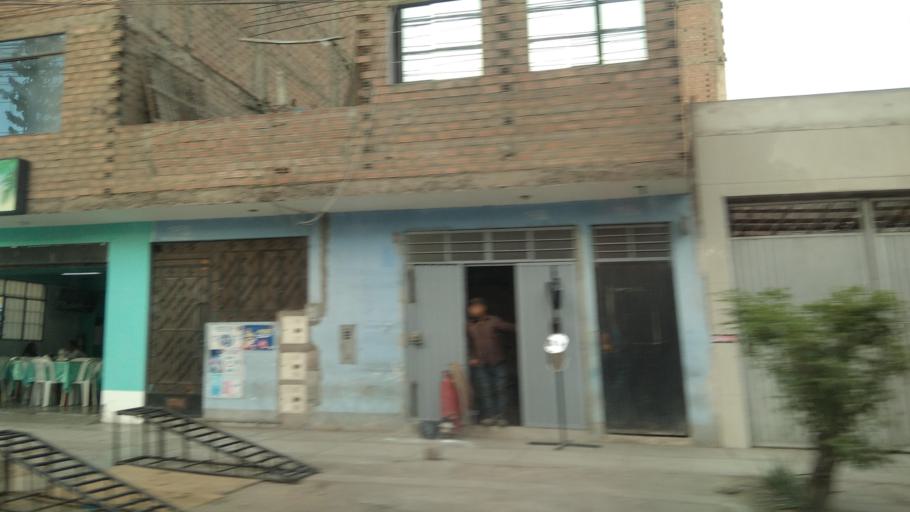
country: PE
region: Lima
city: Lima
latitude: -12.0084
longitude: -77.0000
